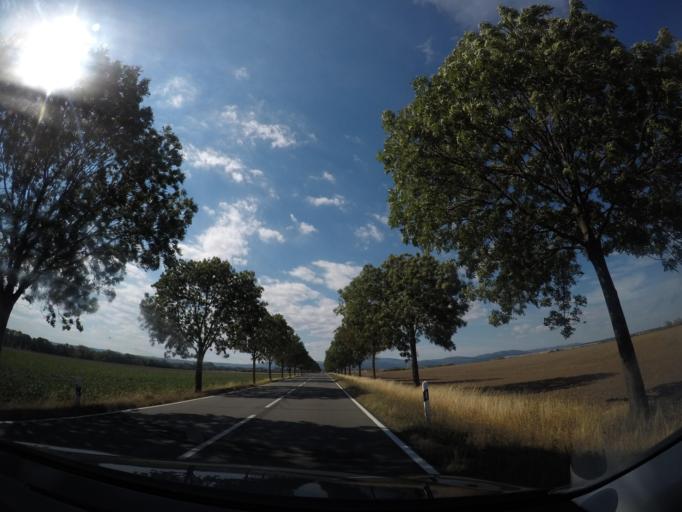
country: DE
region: Saxony-Anhalt
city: Langeln
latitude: 51.9308
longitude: 10.8081
